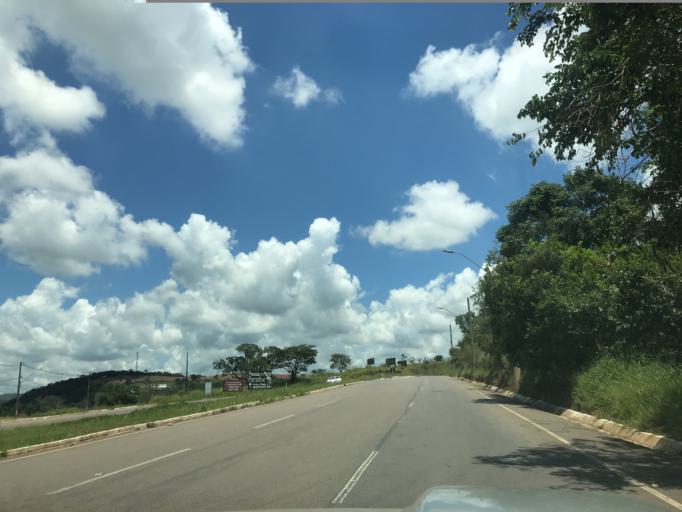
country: BR
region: Minas Gerais
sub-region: Tres Coracoes
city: Tres Coracoes
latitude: -21.6588
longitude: -45.2967
